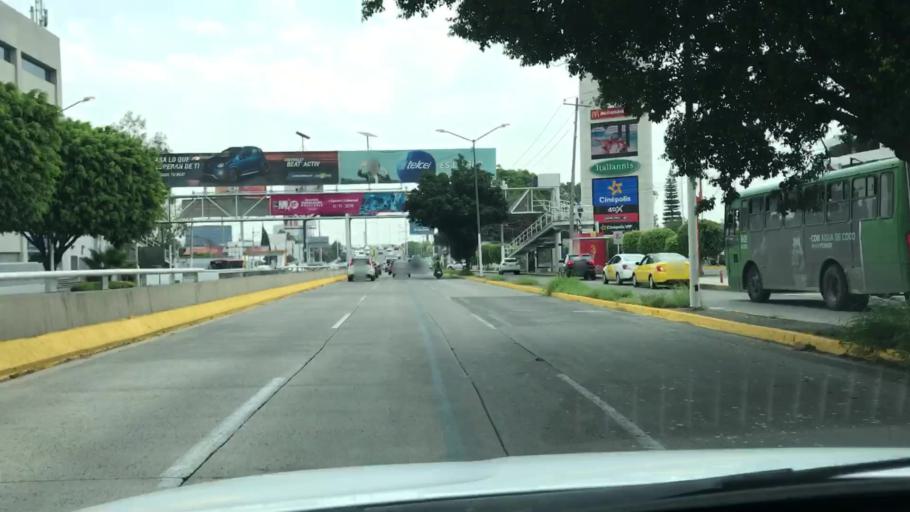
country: MX
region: Jalisco
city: Guadalajara
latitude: 20.6753
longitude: -103.4050
